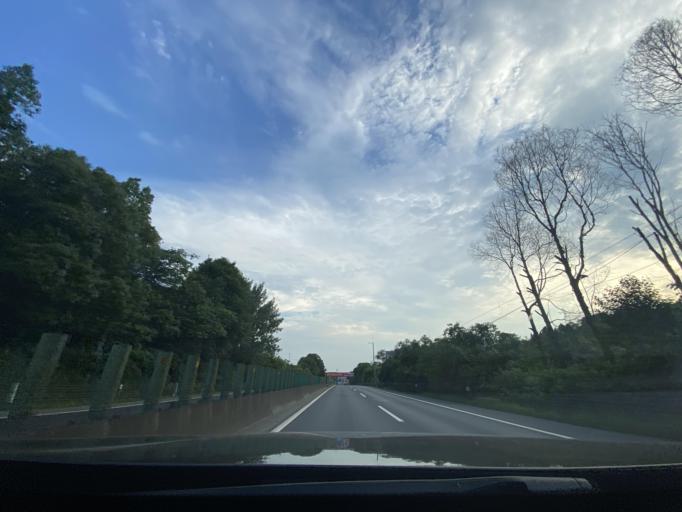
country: CN
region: Sichuan
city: Luojiang
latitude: 31.3933
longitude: 104.5600
